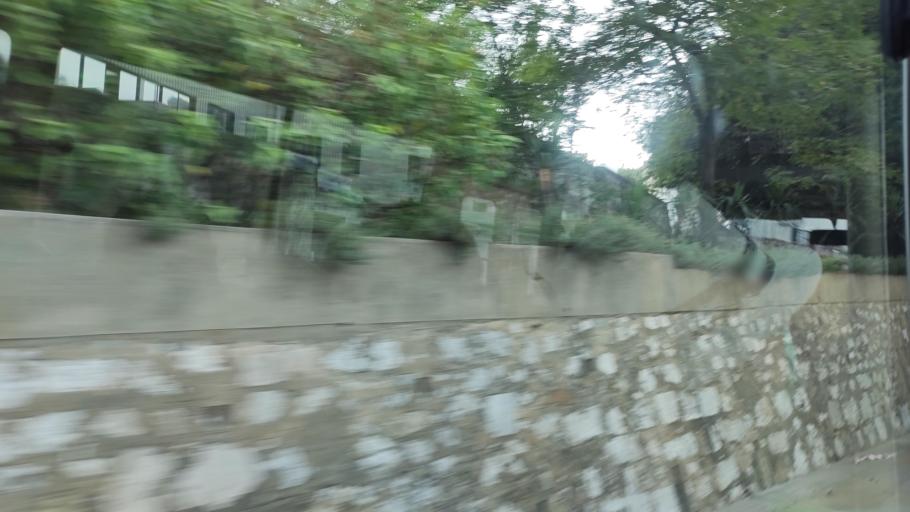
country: GI
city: Gibraltar
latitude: 36.1269
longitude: -5.3520
